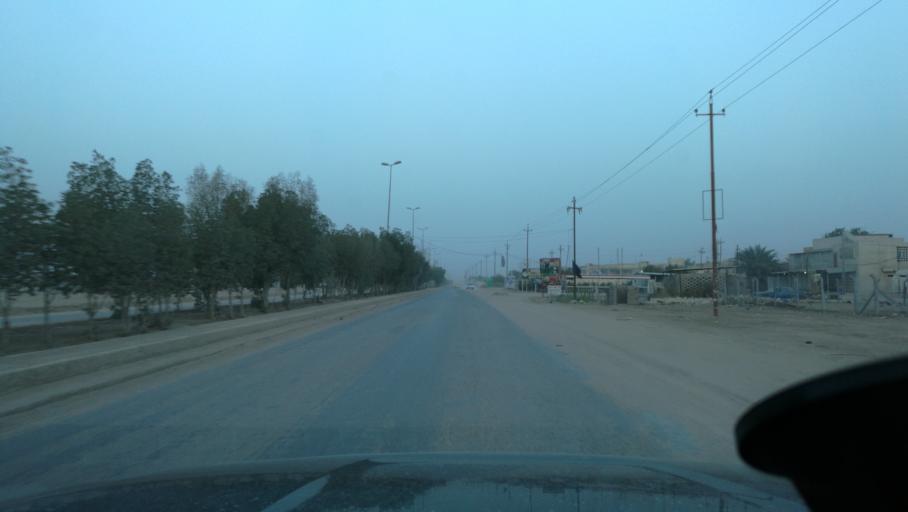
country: IQ
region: Dhi Qar
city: An Nasiriyah
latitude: 31.0252
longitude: 46.2485
